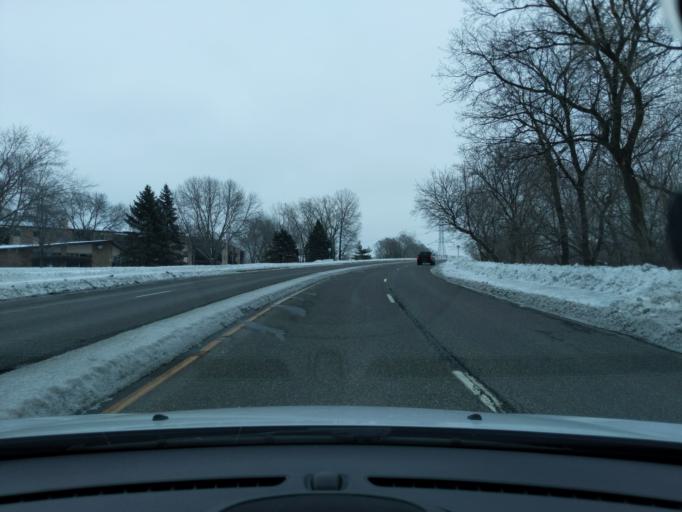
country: US
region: Minnesota
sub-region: Ramsey County
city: Roseville
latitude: 45.0204
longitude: -93.1434
